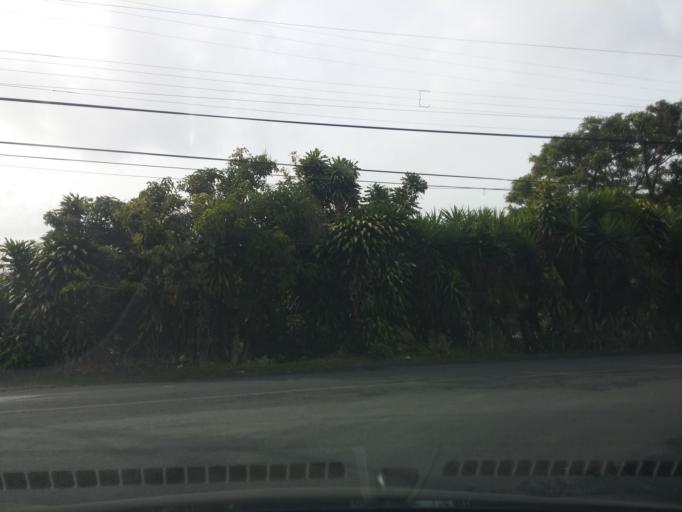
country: CR
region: Heredia
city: Llorente
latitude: 10.0050
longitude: -84.1467
